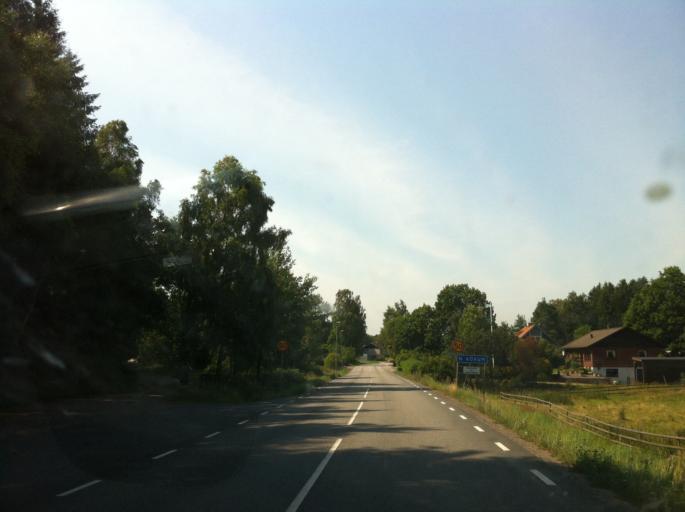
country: SE
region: Skane
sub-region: Hoors Kommun
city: Hoeoer
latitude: 56.0141
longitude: 13.5159
